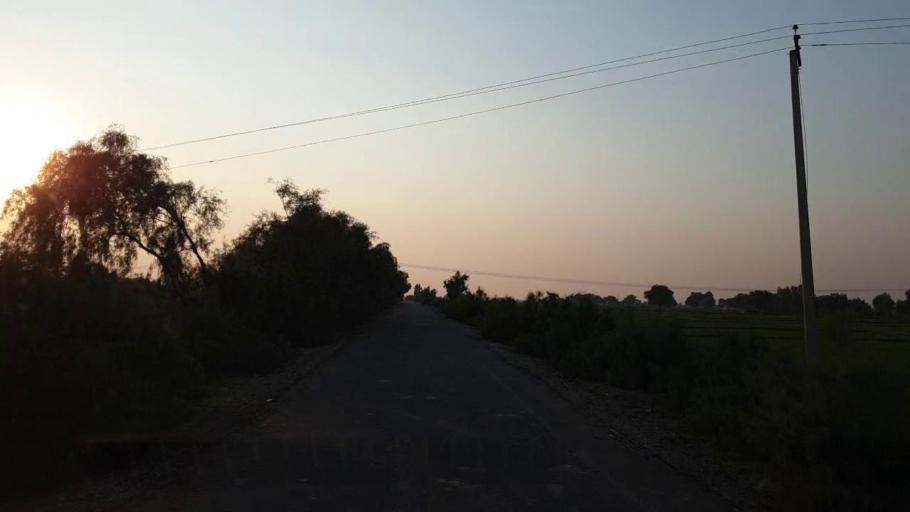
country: PK
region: Sindh
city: Sehwan
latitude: 26.4489
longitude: 67.7666
